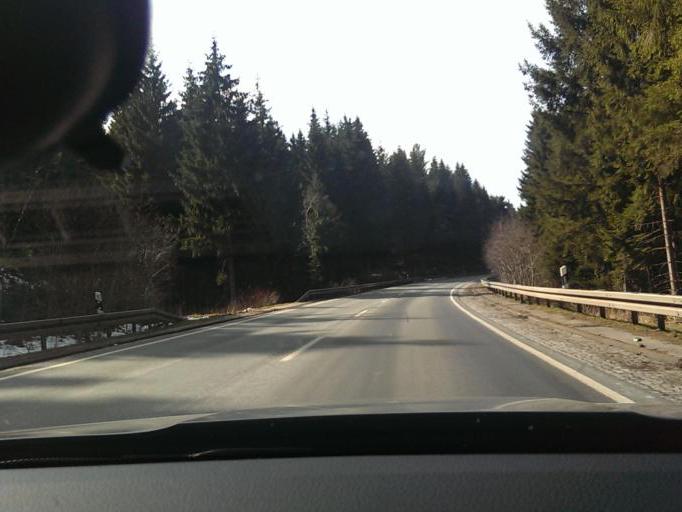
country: DE
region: Thuringia
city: Luisenthal
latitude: 50.7584
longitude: 10.7440
